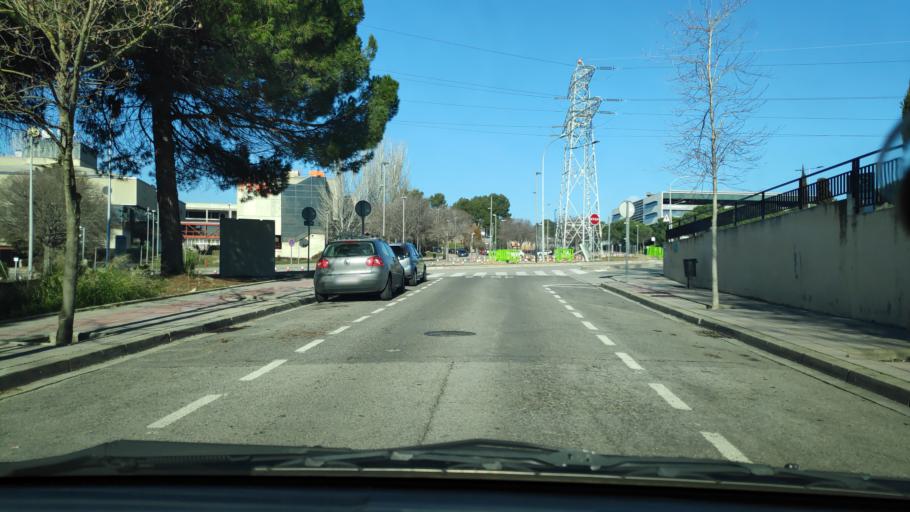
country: ES
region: Catalonia
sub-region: Provincia de Barcelona
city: Sant Cugat del Valles
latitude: 41.4915
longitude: 2.0736
